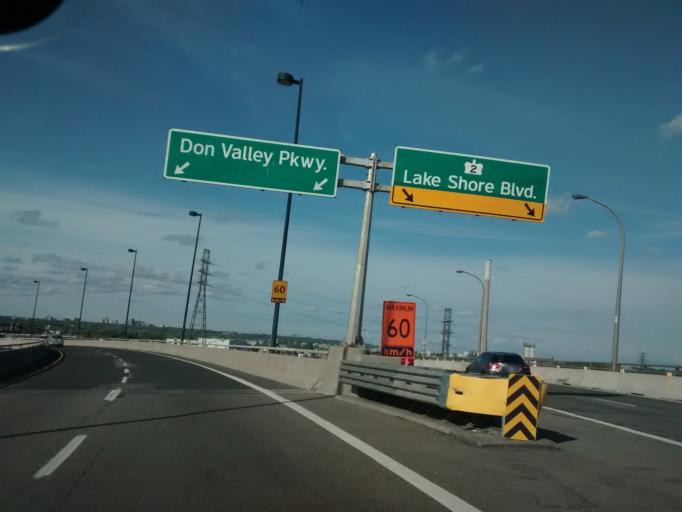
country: CA
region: Ontario
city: Toronto
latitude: 43.6494
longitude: -79.3494
